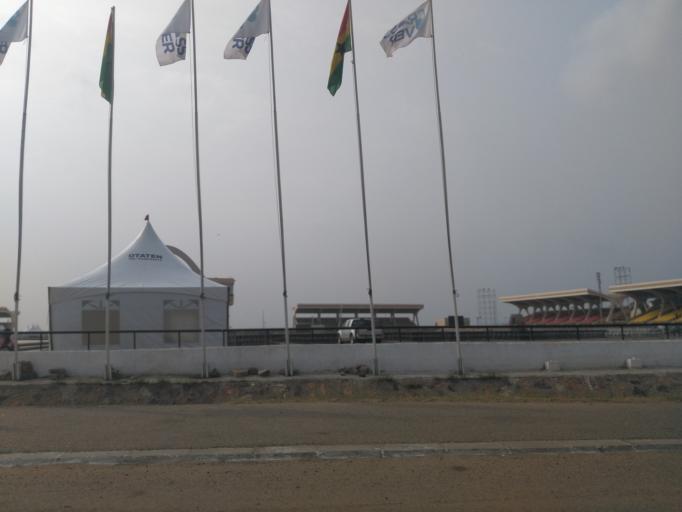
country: GH
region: Greater Accra
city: Accra
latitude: 5.5485
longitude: -0.1929
